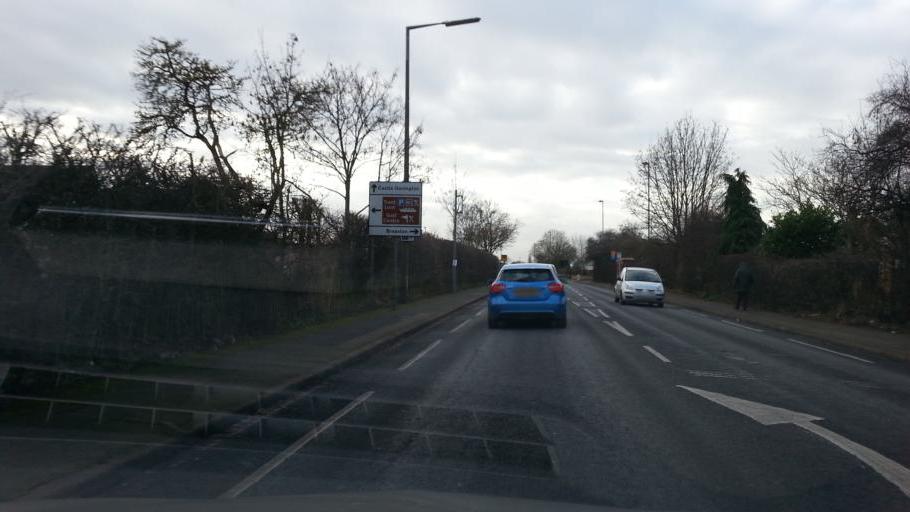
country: GB
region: England
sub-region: Derbyshire
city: Long Eaton
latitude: 52.8810
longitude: -1.2922
